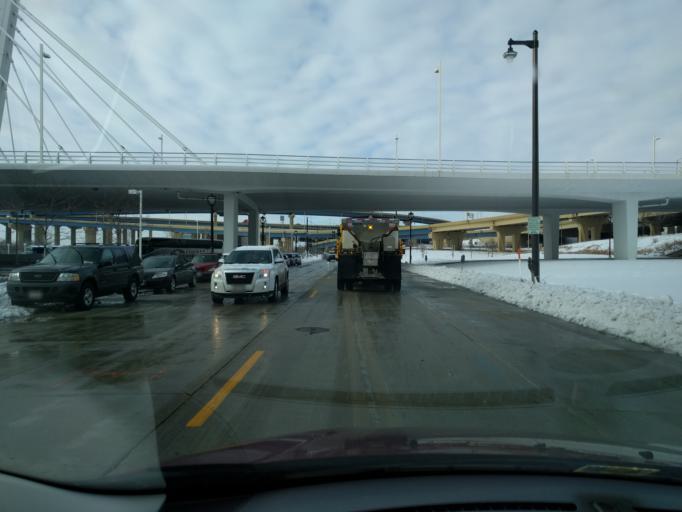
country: US
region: Wisconsin
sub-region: Milwaukee County
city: Milwaukee
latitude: 43.0345
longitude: -87.9179
